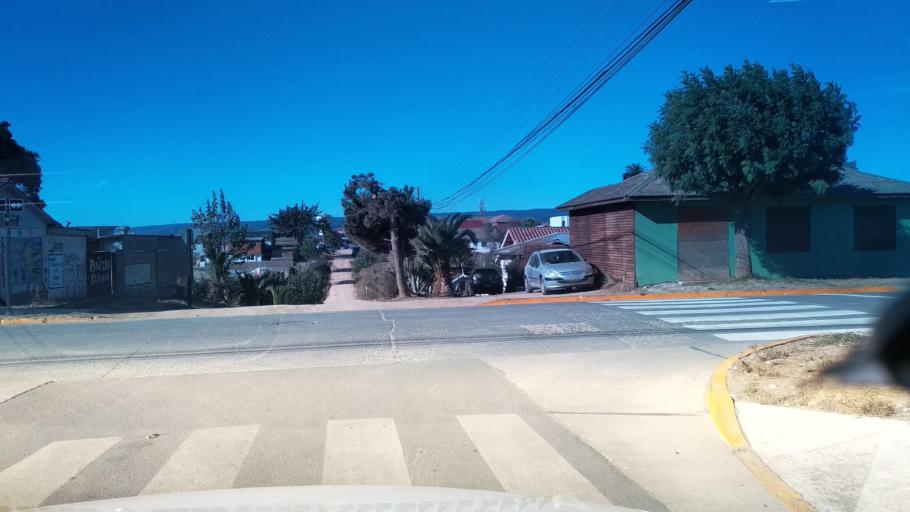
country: CL
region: O'Higgins
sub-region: Provincia de Colchagua
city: Santa Cruz
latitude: -34.3895
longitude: -72.0080
